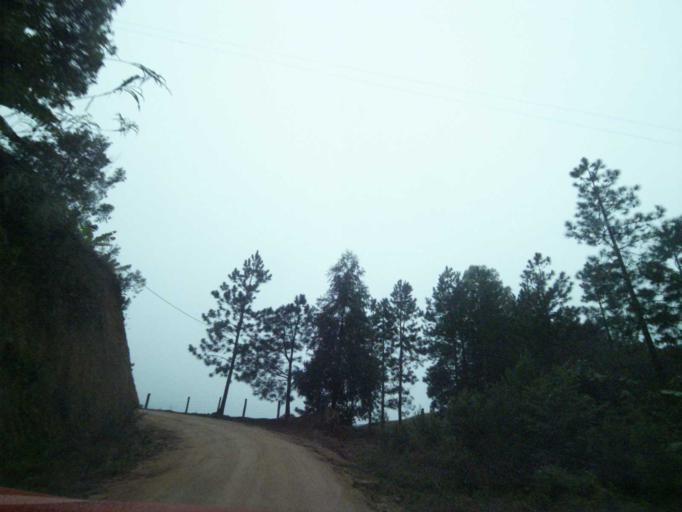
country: BR
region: Santa Catarina
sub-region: Anitapolis
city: Anitapolis
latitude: -27.9145
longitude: -49.0965
